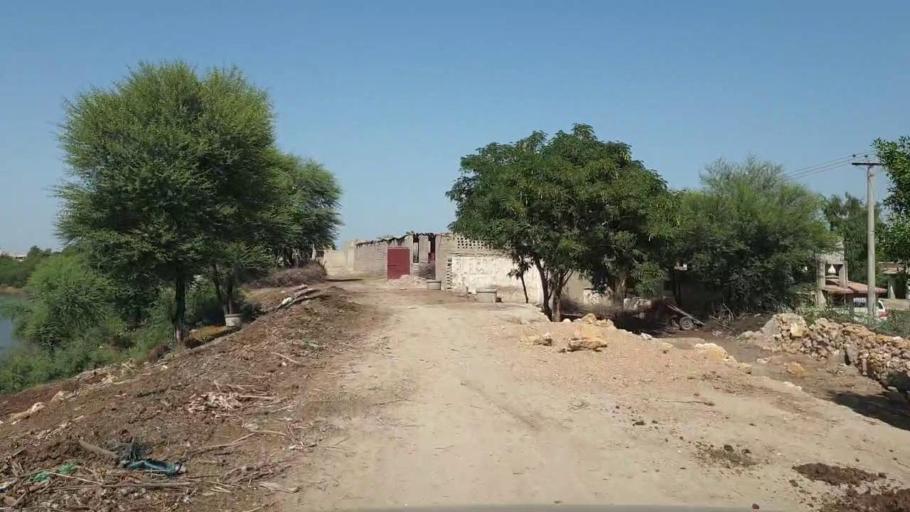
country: PK
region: Sindh
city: Matiari
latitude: 25.6301
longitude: 68.4900
